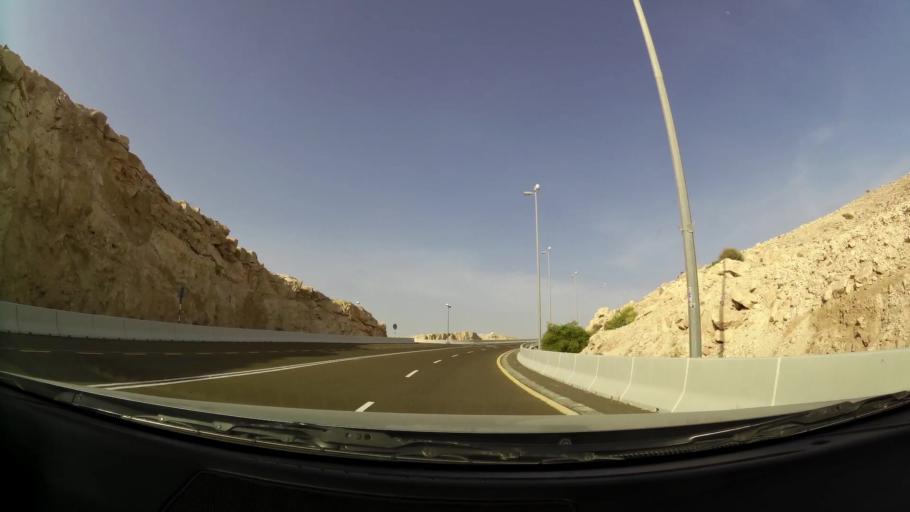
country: AE
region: Abu Dhabi
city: Al Ain
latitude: 24.0834
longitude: 55.7643
